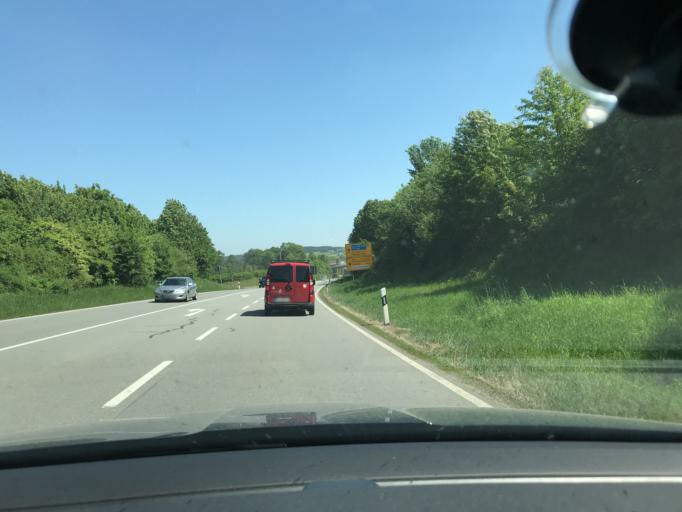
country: DE
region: Saxony
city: Zwonitz
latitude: 50.6394
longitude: 12.8215
